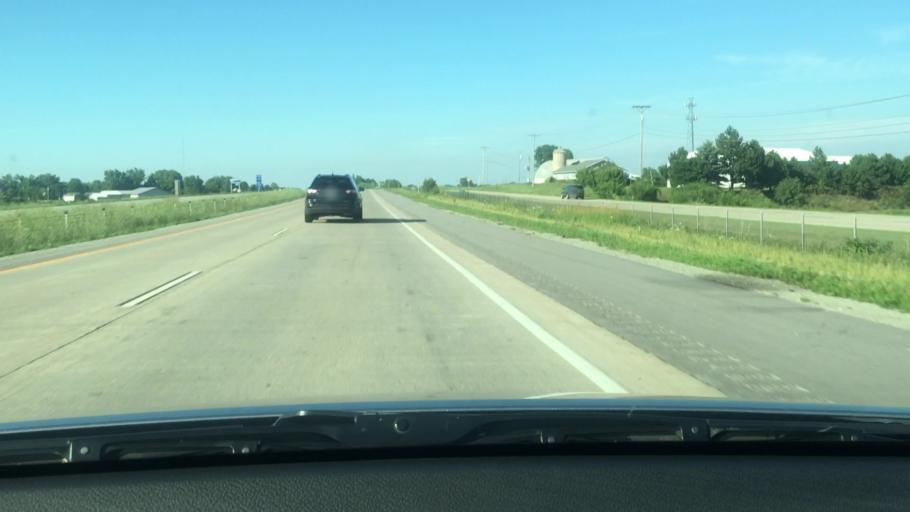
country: US
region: Wisconsin
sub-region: Brown County
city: Wrightstown
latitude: 44.3257
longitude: -88.2134
